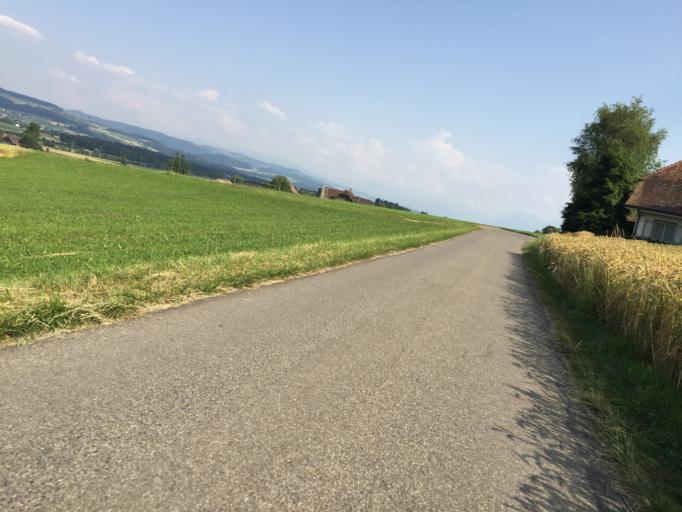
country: CH
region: Bern
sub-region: Bern-Mittelland District
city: Rubigen
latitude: 46.9204
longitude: 7.5222
